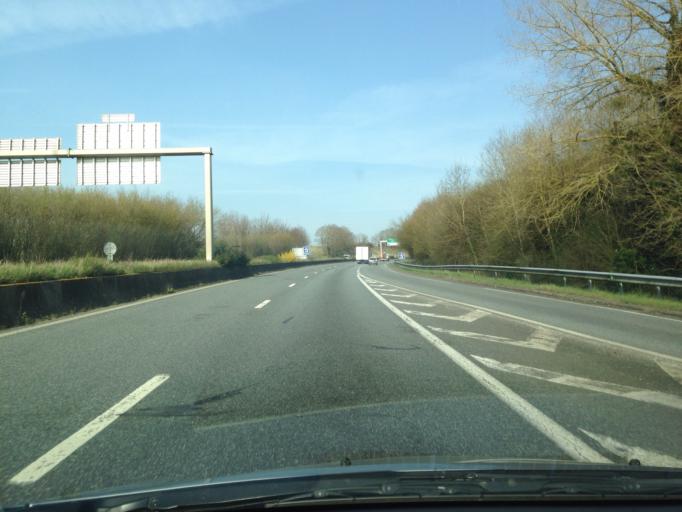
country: FR
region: Picardie
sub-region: Departement de la Somme
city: Abbeville
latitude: 50.1287
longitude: 1.8005
